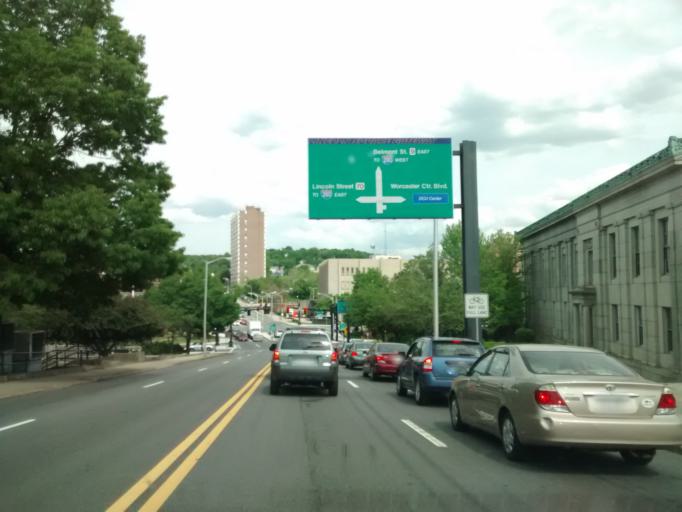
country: US
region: Massachusetts
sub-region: Worcester County
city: Worcester
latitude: 42.2714
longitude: -71.8010
